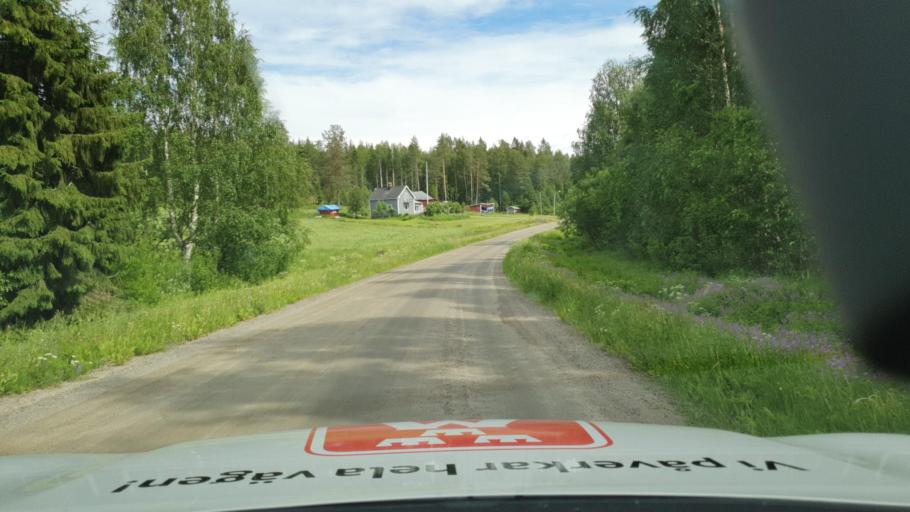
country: SE
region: Vaesterbotten
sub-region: Skelleftea Kommun
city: Burtraesk
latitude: 64.4926
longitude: 20.5939
